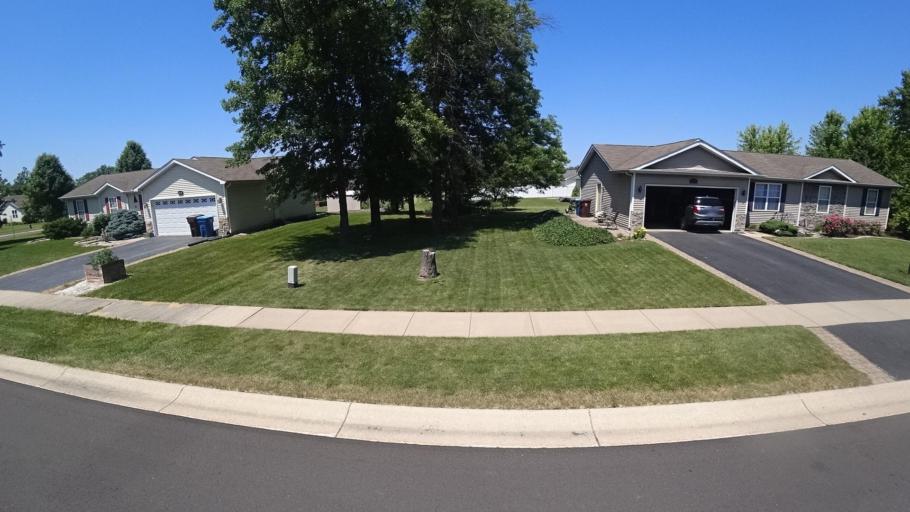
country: US
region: Indiana
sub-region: Porter County
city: Burns Harbor
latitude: 41.6016
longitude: -87.1373
